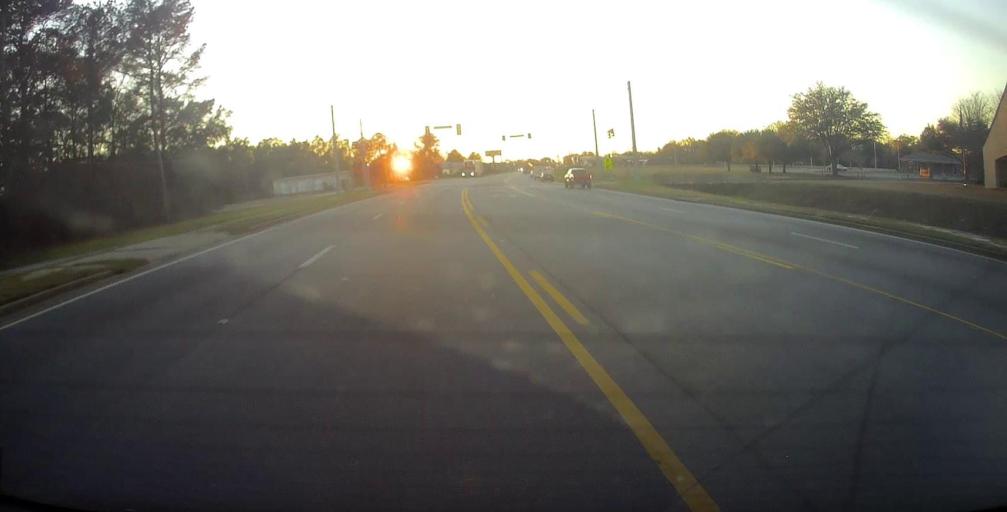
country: US
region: Georgia
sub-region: Dougherty County
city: Albany
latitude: 31.5491
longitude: -84.1710
